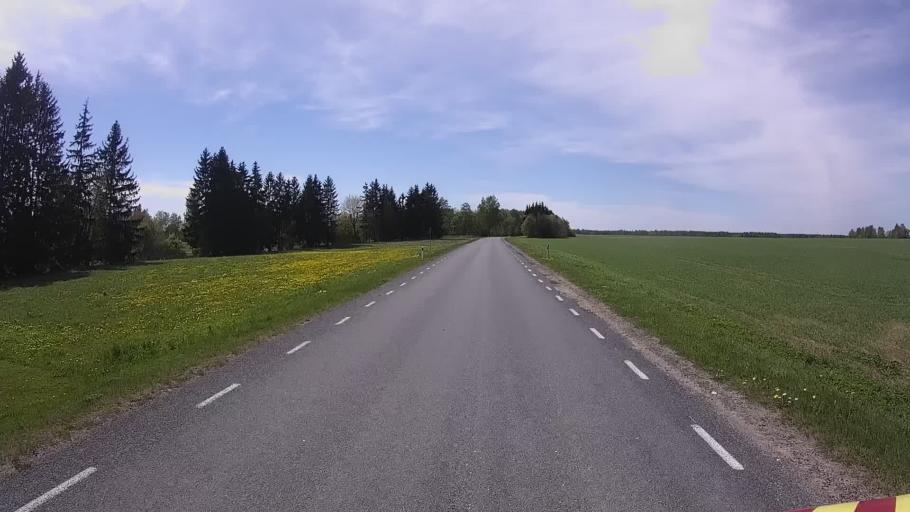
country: LV
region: Apes Novads
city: Ape
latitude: 57.6062
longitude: 26.5482
